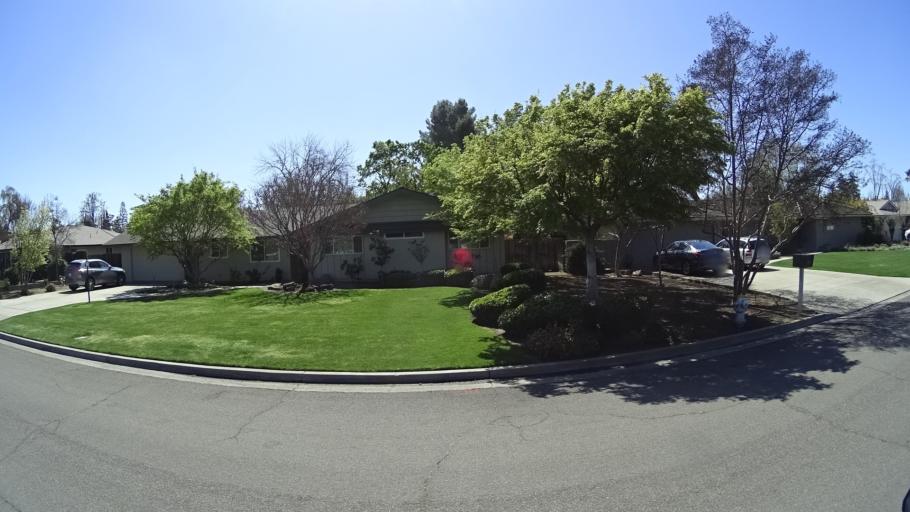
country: US
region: California
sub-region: Fresno County
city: Fresno
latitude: 36.8147
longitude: -119.8106
